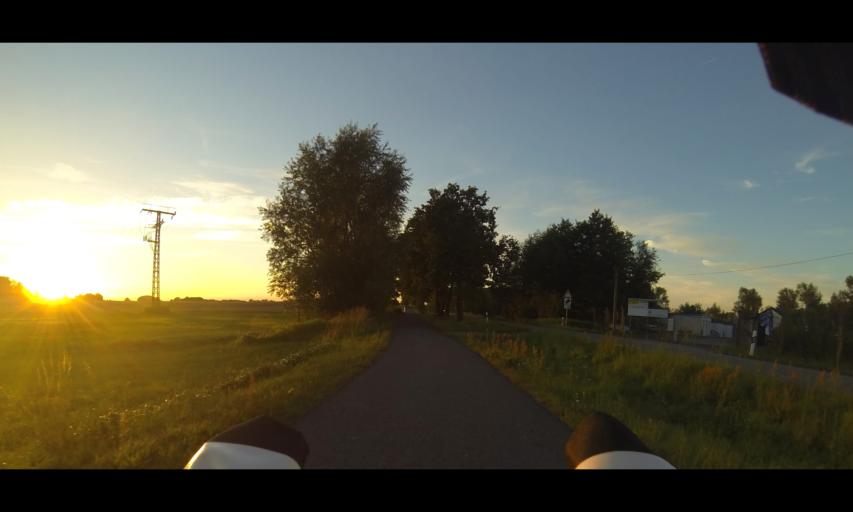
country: DE
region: Saxony
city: Moritzburg
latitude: 51.1704
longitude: 13.7210
